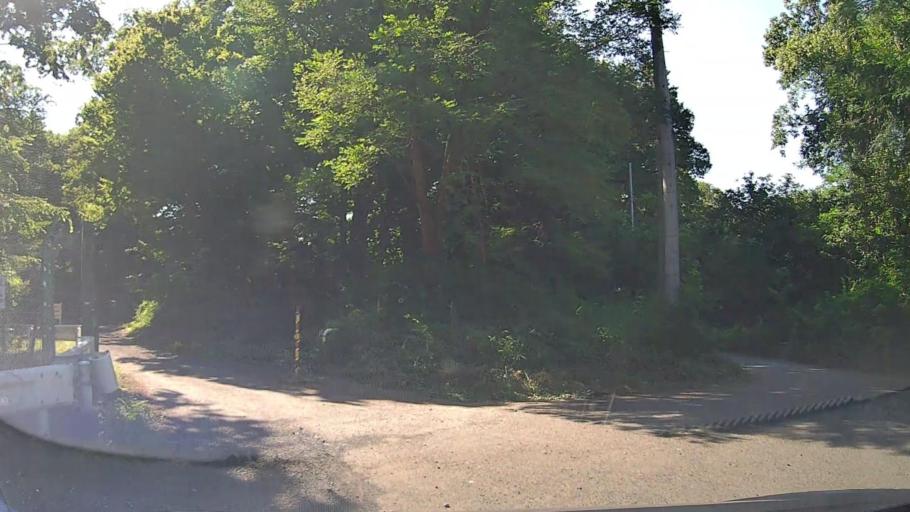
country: JP
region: Saitama
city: Sayama
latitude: 35.7830
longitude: 139.3983
